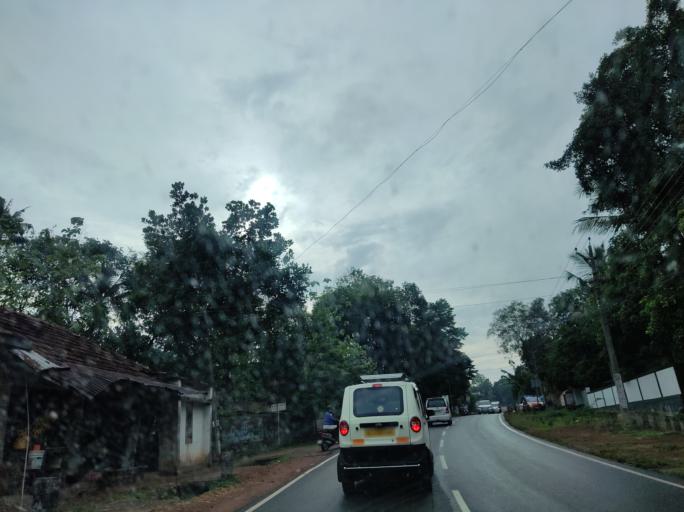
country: IN
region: Kerala
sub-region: Pattanamtitta
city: Adur
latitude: 9.1705
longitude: 76.6523
